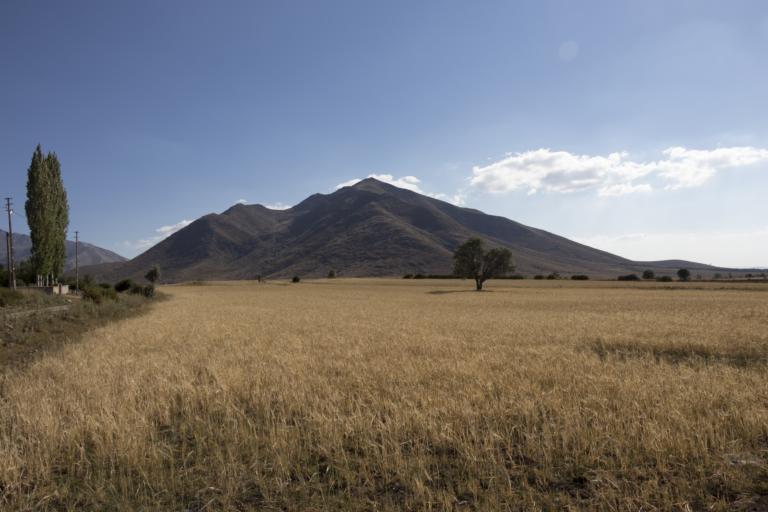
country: TR
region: Kayseri
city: Toklar
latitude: 38.4040
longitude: 36.0816
